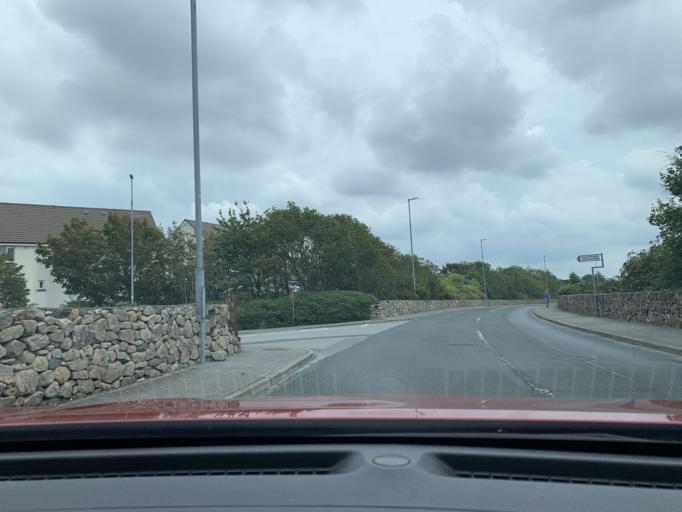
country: IE
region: Connaught
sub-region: County Galway
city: Gaillimh
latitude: 53.2765
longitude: -9.0932
